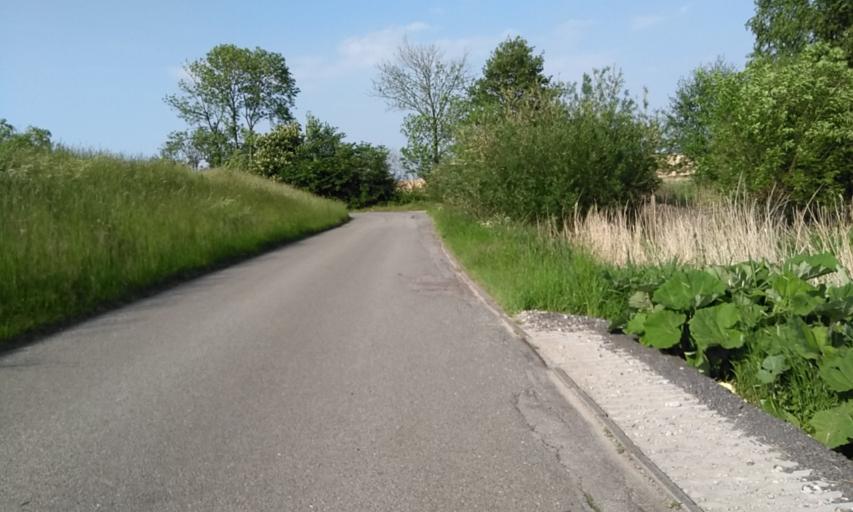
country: DE
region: Lower Saxony
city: Buxtehude
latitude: 53.4850
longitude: 9.7090
